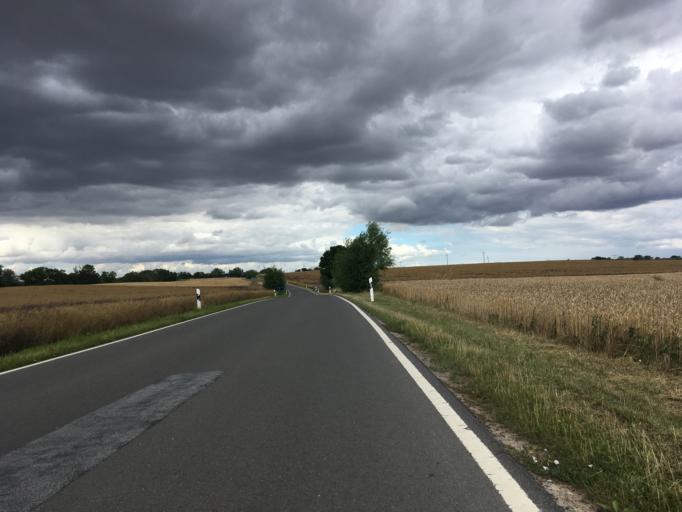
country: DE
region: Brandenburg
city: Gramzow
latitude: 53.2222
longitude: 13.9381
